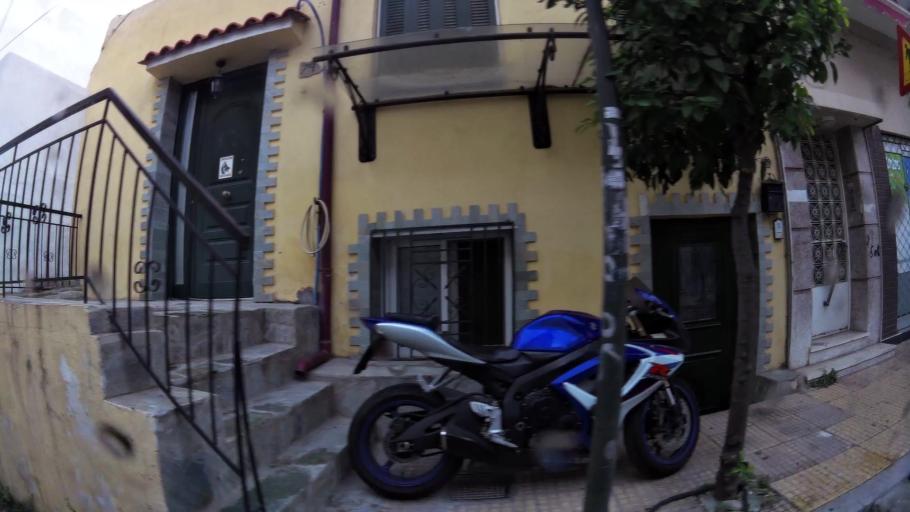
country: GR
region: Attica
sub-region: Nomos Piraios
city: Nikaia
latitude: 37.9598
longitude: 23.6422
